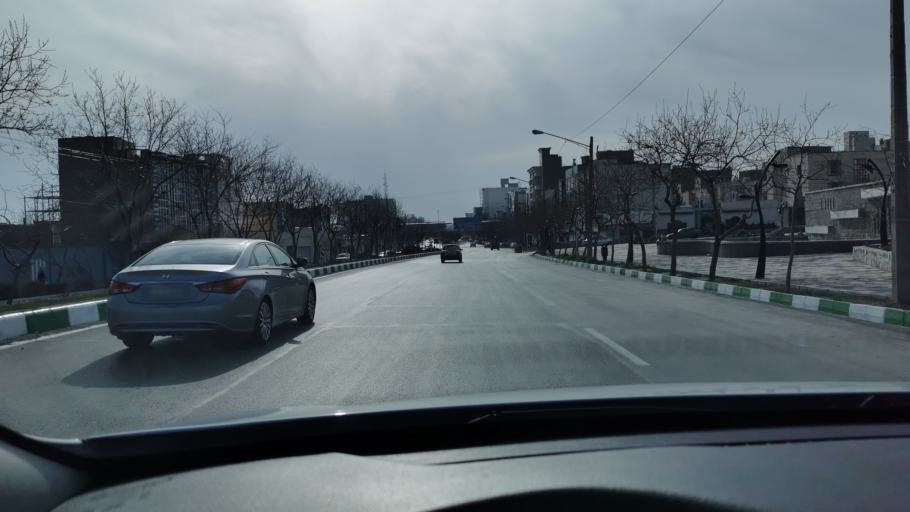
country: IR
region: Razavi Khorasan
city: Mashhad
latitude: 36.2941
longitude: 59.5323
